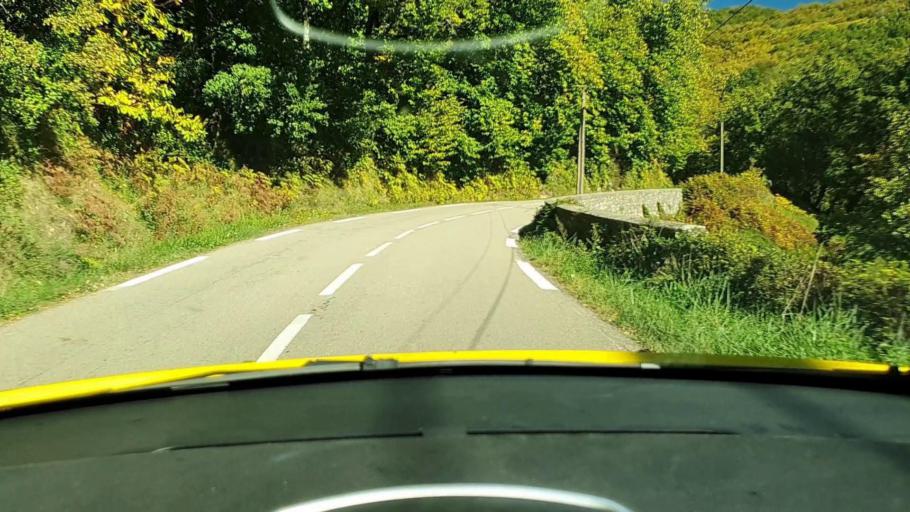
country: FR
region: Languedoc-Roussillon
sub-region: Departement du Gard
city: Le Vigan
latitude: 43.9686
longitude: 3.4151
